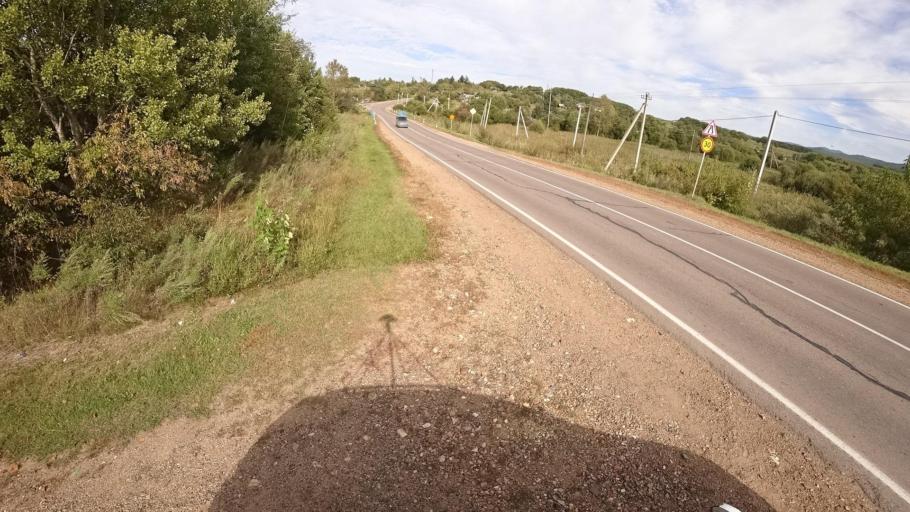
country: RU
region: Primorskiy
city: Dostoyevka
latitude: 44.3202
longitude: 133.4741
